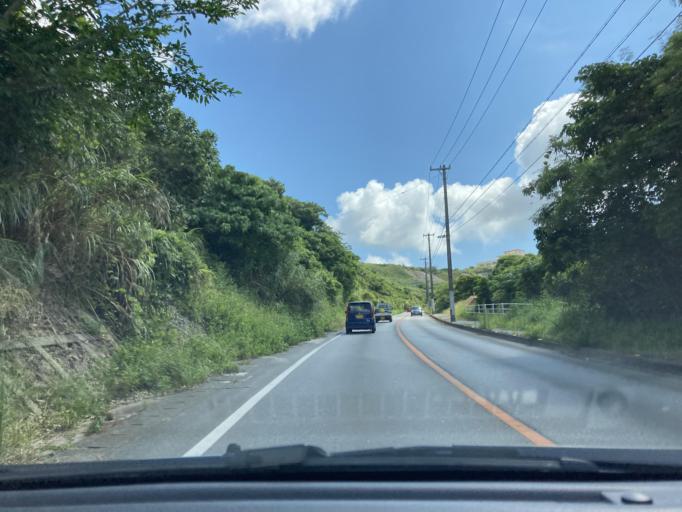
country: JP
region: Okinawa
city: Tomigusuku
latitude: 26.1615
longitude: 127.7673
